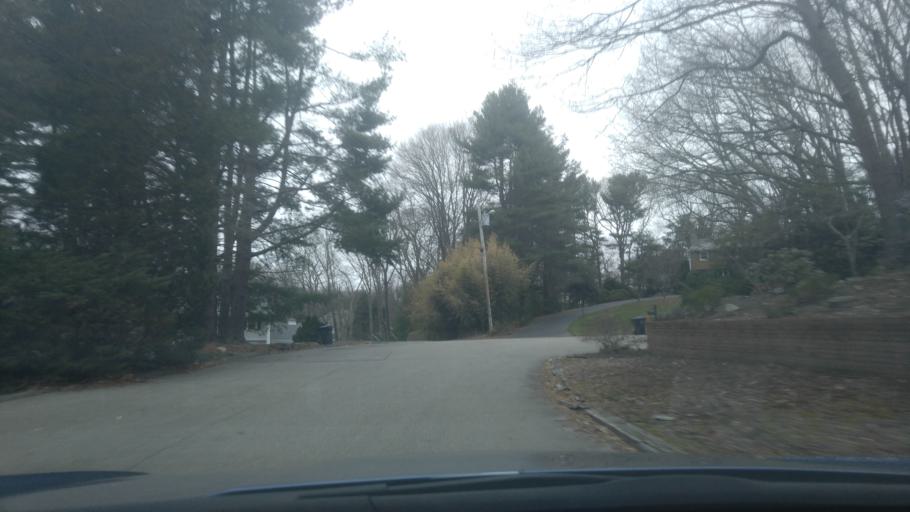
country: US
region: Rhode Island
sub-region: Kent County
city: East Greenwich
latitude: 41.6691
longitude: -71.4644
